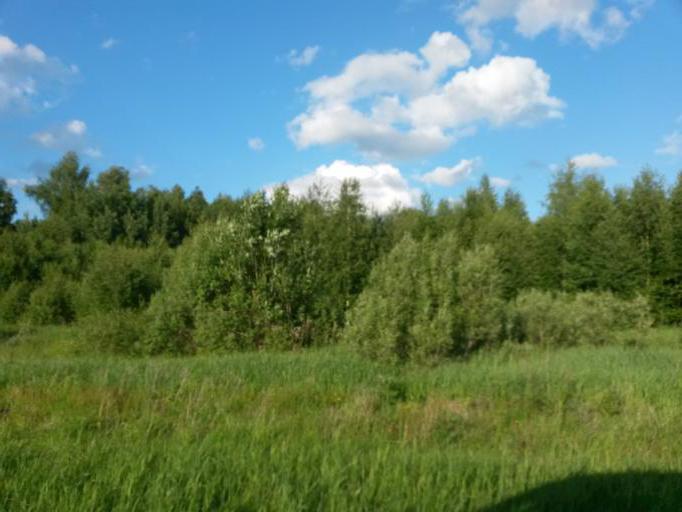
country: RU
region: Jaroslavl
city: Burmakino
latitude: 57.3688
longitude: 40.2018
